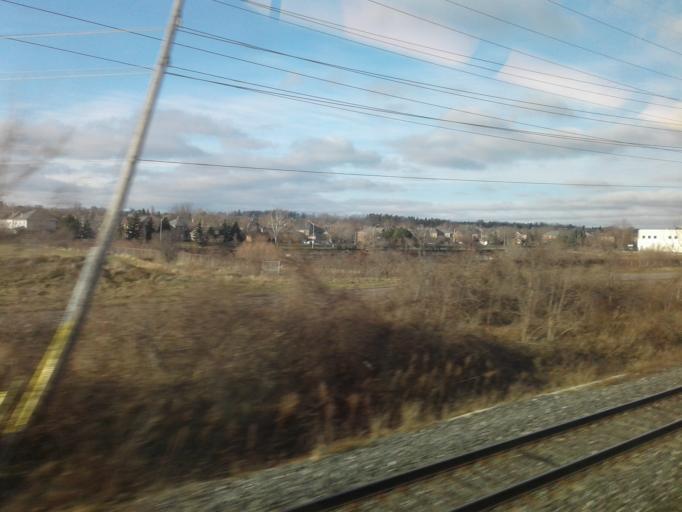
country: CA
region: Ontario
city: Oakville
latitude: 43.4920
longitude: -79.6524
